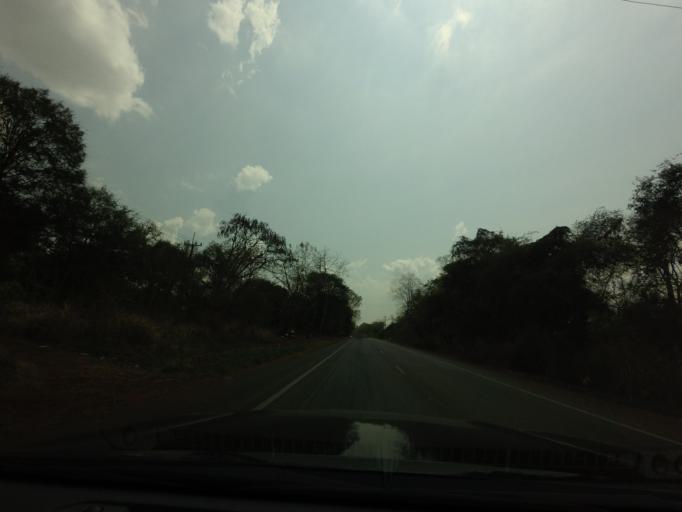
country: TH
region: Kanchanaburi
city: Sai Yok
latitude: 14.1415
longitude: 99.1477
